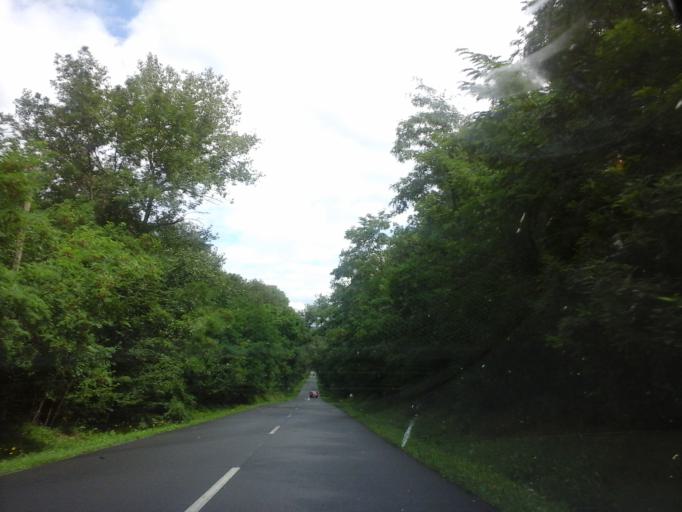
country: HU
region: Borsod-Abauj-Zemplen
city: Rudabanya
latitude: 48.4588
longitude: 20.4892
